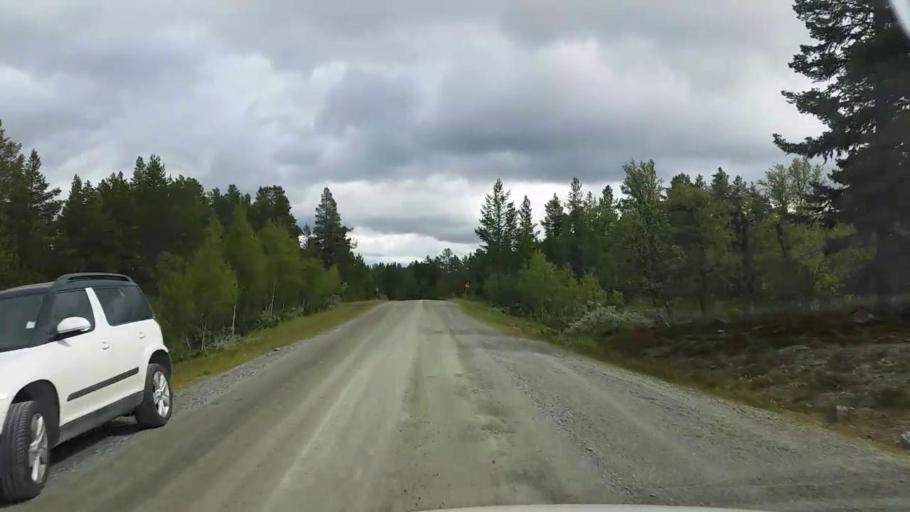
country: NO
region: Hedmark
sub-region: Engerdal
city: Engerdal
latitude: 62.3326
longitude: 12.6388
